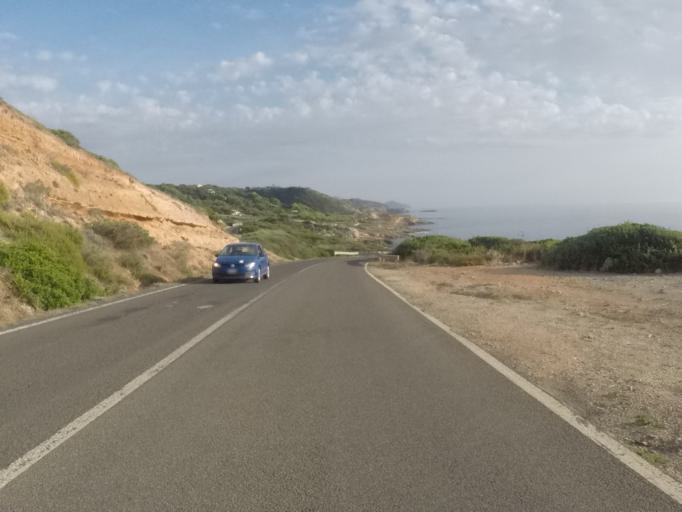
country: IT
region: Sardinia
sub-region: Provincia di Sassari
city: Alghero
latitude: 40.5271
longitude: 8.3304
